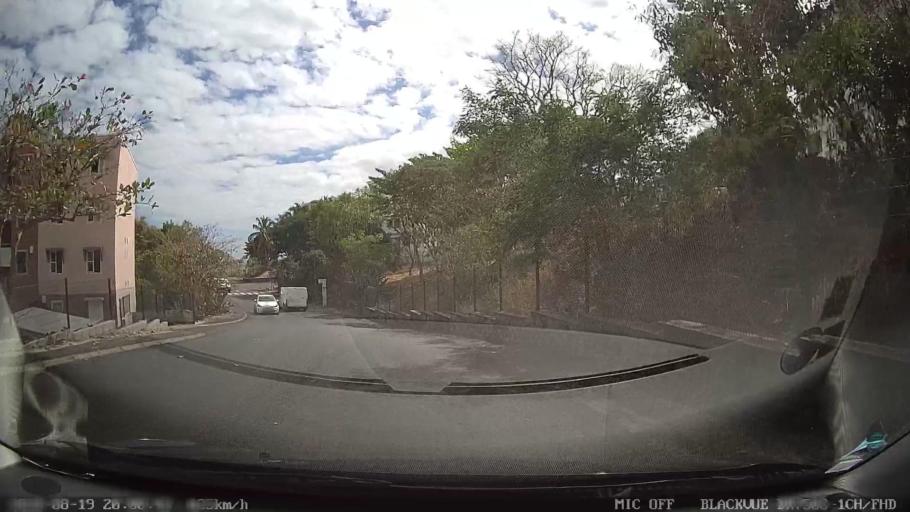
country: RE
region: Reunion
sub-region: Reunion
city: La Possession
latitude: -20.9522
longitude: 55.3323
